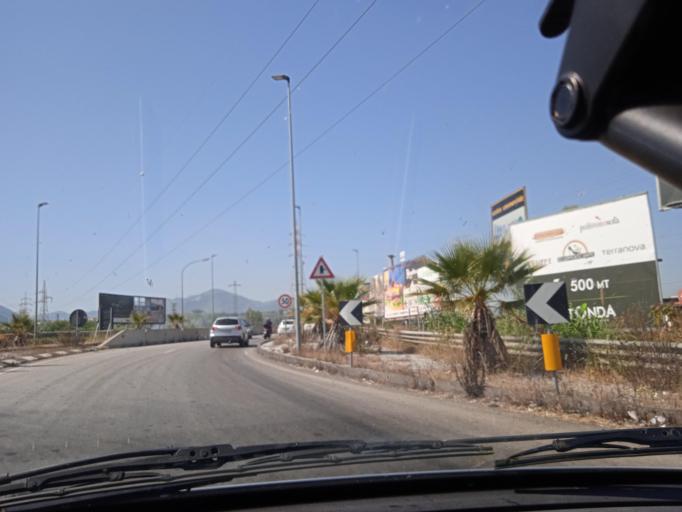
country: IT
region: Sicily
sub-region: Messina
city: San Filippo del Mela
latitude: 38.1885
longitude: 15.2731
